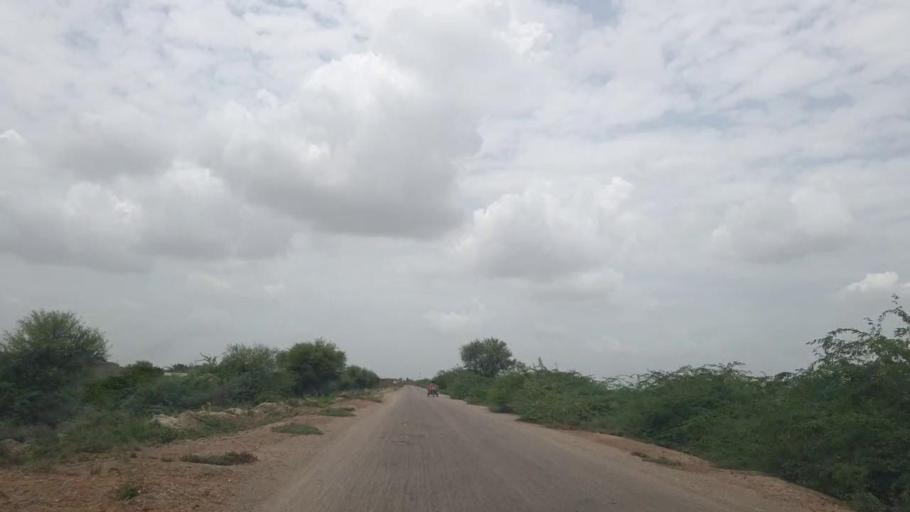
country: PK
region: Sindh
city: Naukot
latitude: 24.9229
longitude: 69.2738
